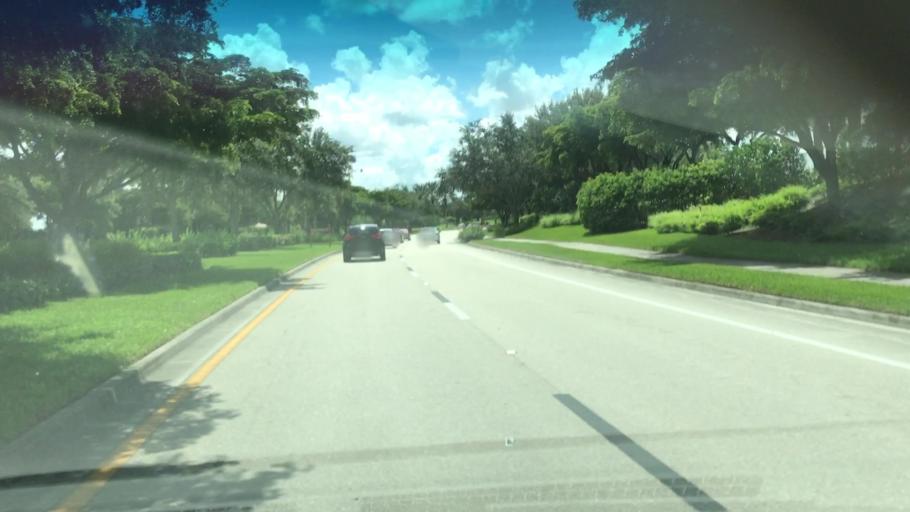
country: US
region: Florida
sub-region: Lee County
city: Estero
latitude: 26.4110
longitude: -81.7836
